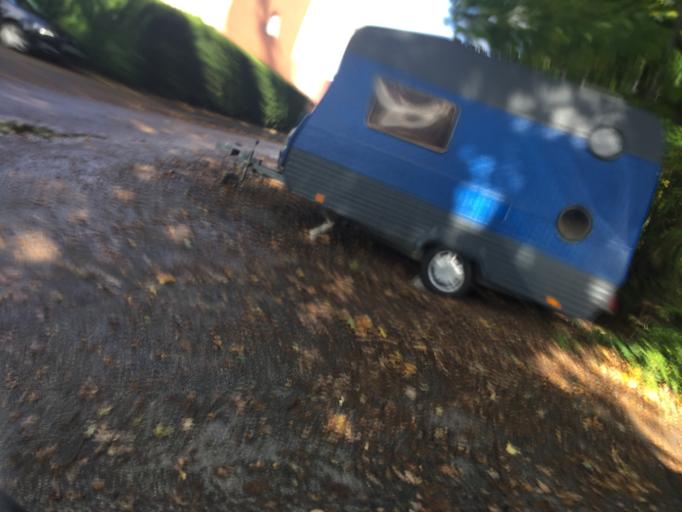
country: DE
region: Schleswig-Holstein
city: Heiligenstedten
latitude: 53.9331
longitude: 9.4962
